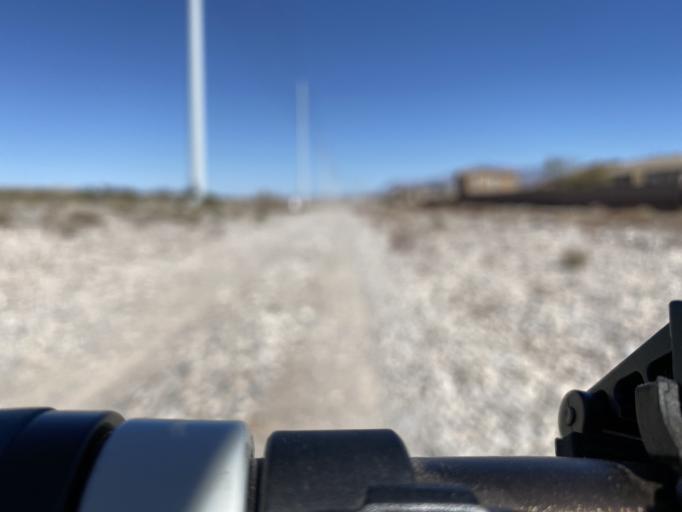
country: US
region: Nevada
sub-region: Clark County
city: Summerlin South
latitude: 36.2977
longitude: -115.3335
